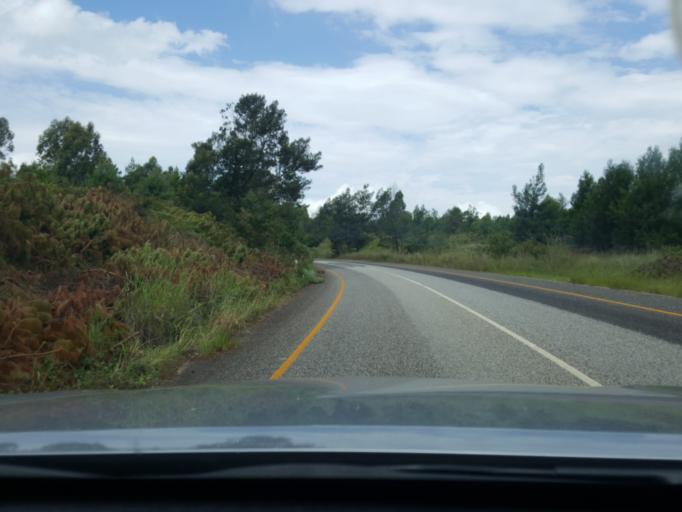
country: ZA
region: Mpumalanga
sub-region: Ehlanzeni District
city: White River
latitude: -25.1840
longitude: 30.8468
